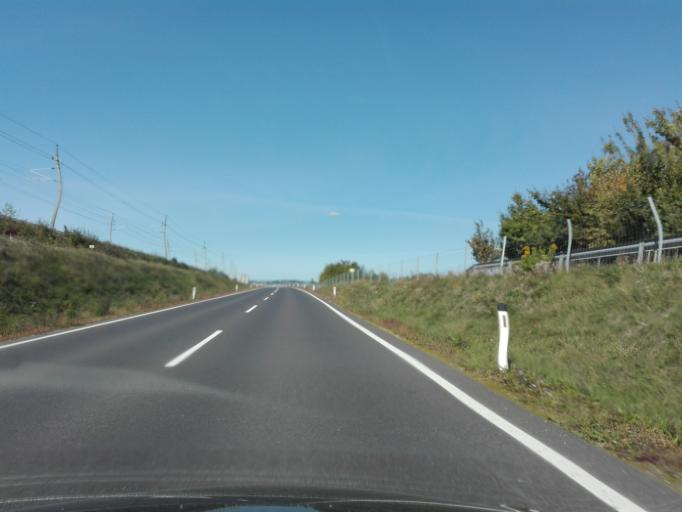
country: AT
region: Lower Austria
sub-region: Politischer Bezirk Amstetten
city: Ennsdorf
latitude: 48.2094
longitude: 14.5085
